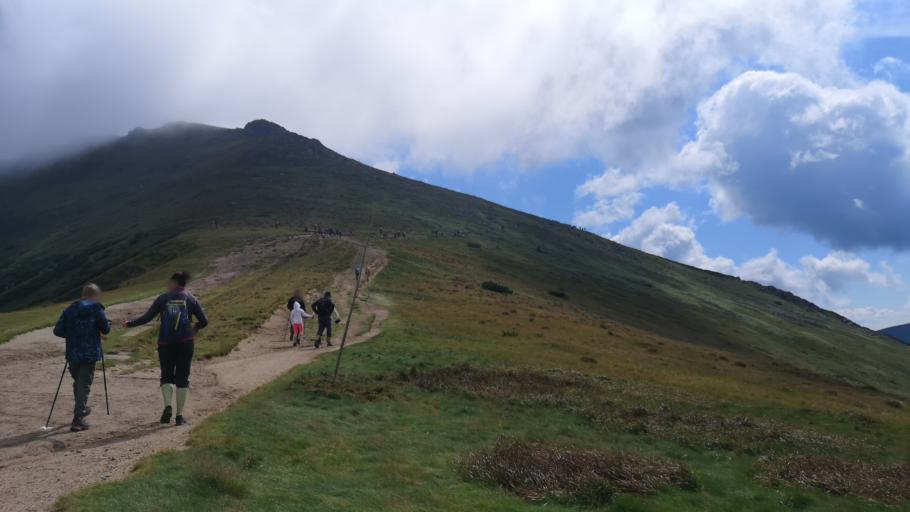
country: SK
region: Banskobystricky
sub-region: Okres Banska Bystrica
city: Brezno
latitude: 48.9399
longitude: 19.6196
